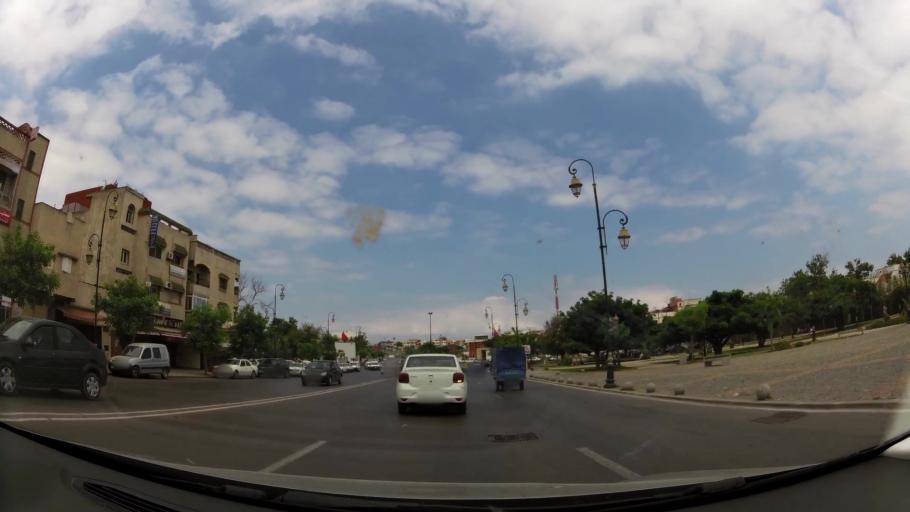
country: MA
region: Rabat-Sale-Zemmour-Zaer
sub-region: Skhirate-Temara
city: Temara
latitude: 33.9758
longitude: -6.8859
